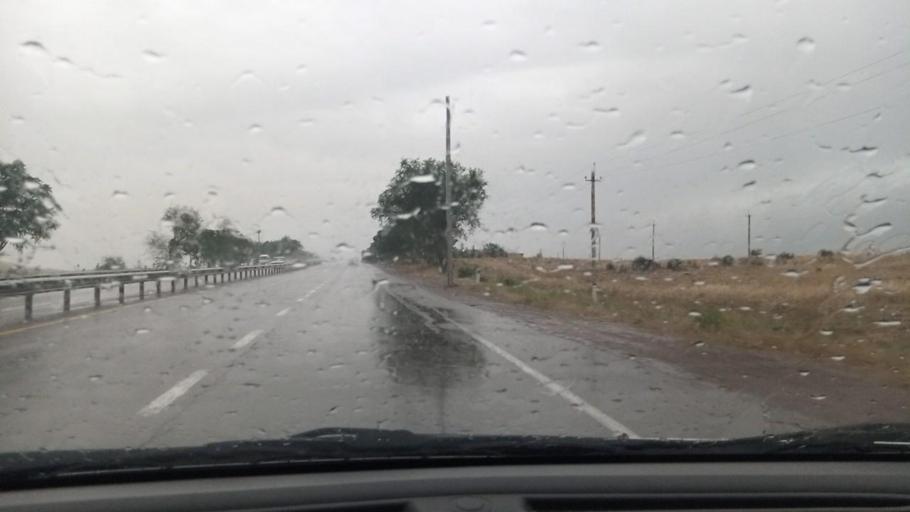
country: UZ
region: Toshkent
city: Ohangaron
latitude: 40.9859
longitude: 69.5366
